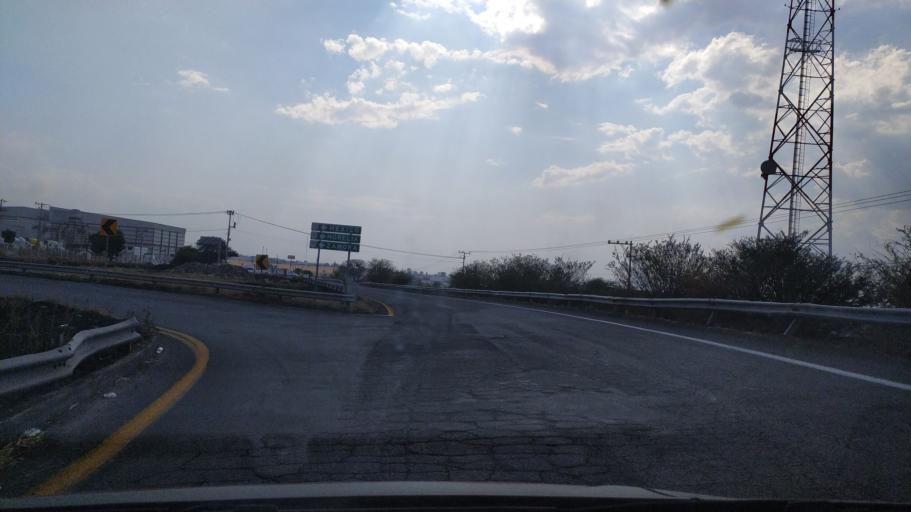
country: MX
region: Michoacan
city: Vistahermosa de Negrete
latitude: 20.2689
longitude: -102.4462
